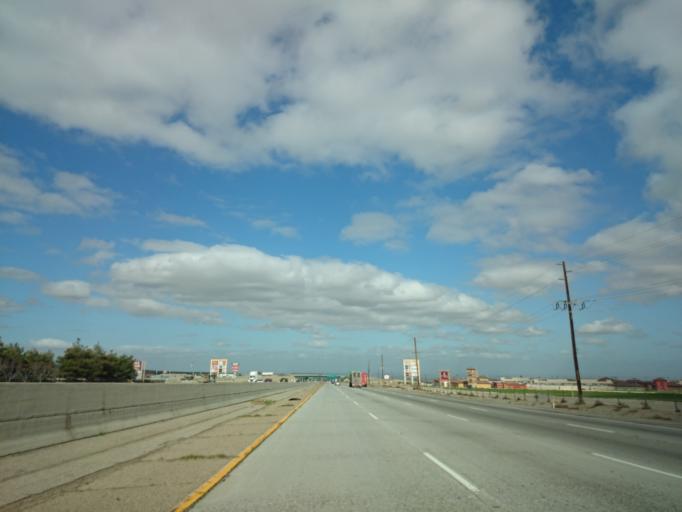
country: US
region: California
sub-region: Kern County
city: Frazier Park
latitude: 34.9801
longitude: -118.9433
